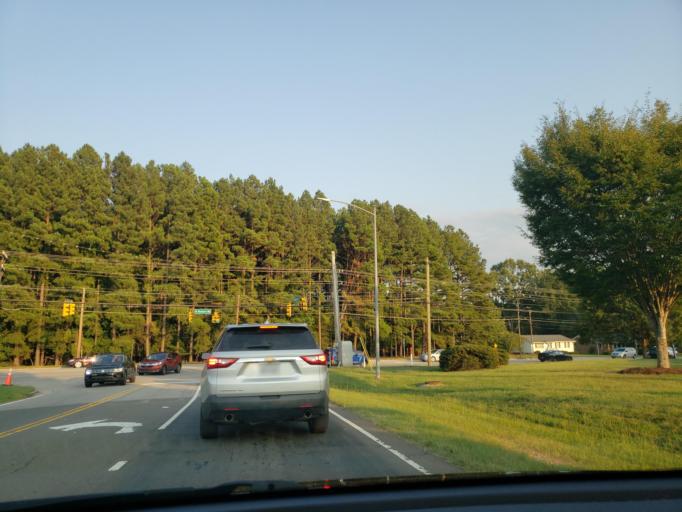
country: US
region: North Carolina
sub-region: Durham County
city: Durham
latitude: 36.0862
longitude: -78.9115
